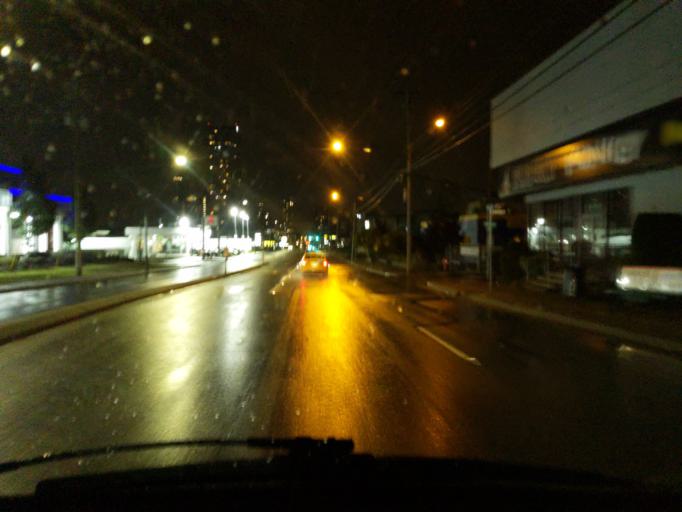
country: CA
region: British Columbia
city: New Westminster
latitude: 49.1916
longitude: -122.8380
